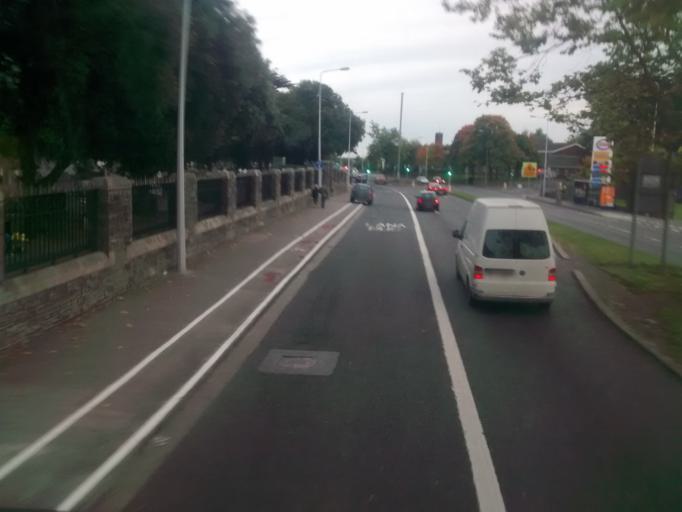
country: IE
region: Leinster
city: Cabra
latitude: 53.3735
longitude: -6.2846
